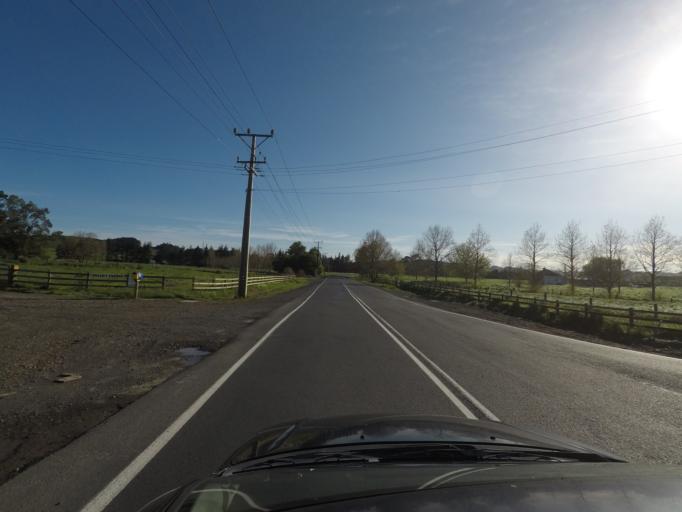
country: NZ
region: Auckland
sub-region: Auckland
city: Red Hill
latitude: -37.0045
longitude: 174.9559
